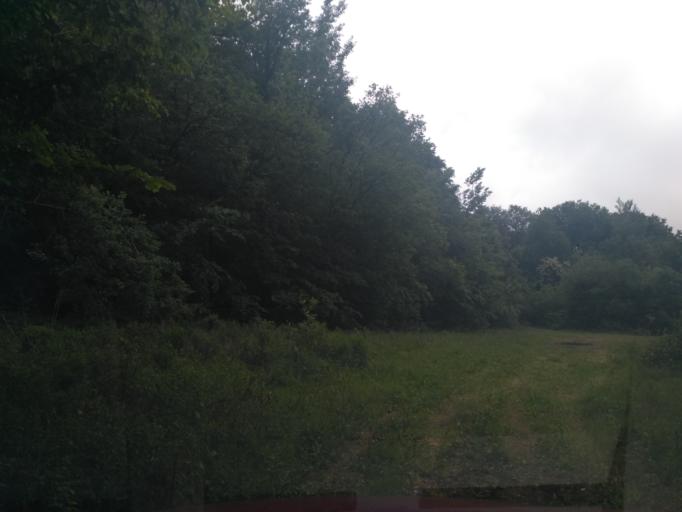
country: SK
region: Kosicky
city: Moldava nad Bodvou
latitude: 48.6950
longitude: 21.0767
